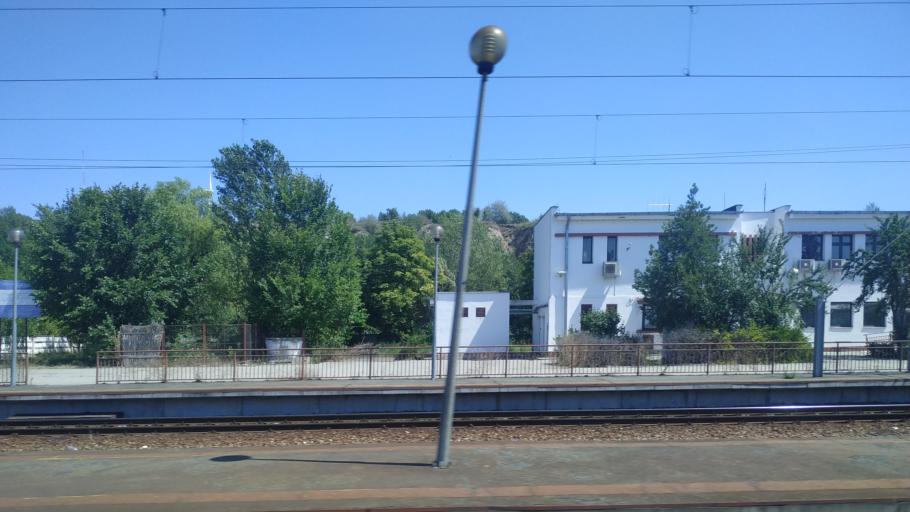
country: RO
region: Constanta
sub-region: Comuna Saligny
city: Saligny
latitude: 44.2892
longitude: 28.0765
